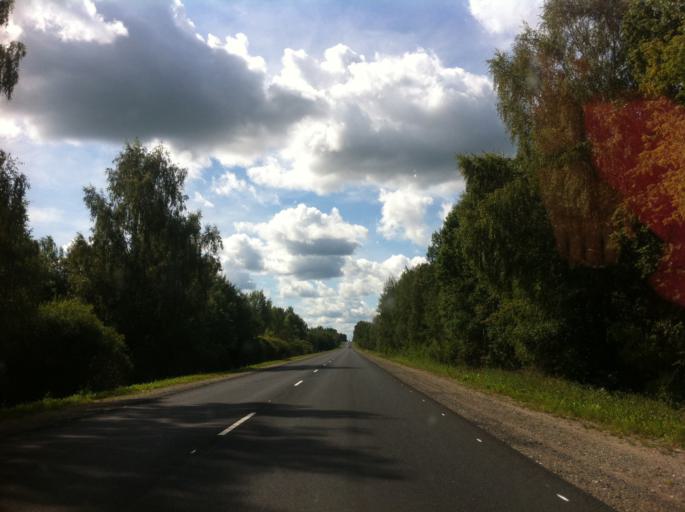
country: RU
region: Pskov
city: Izborsk
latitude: 57.7237
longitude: 27.9464
